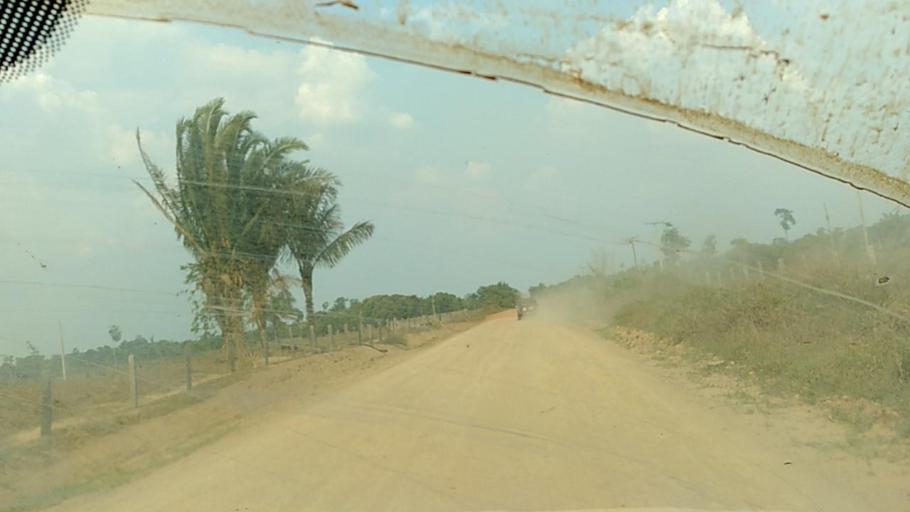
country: BR
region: Rondonia
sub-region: Porto Velho
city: Porto Velho
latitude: -8.6831
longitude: -63.2338
